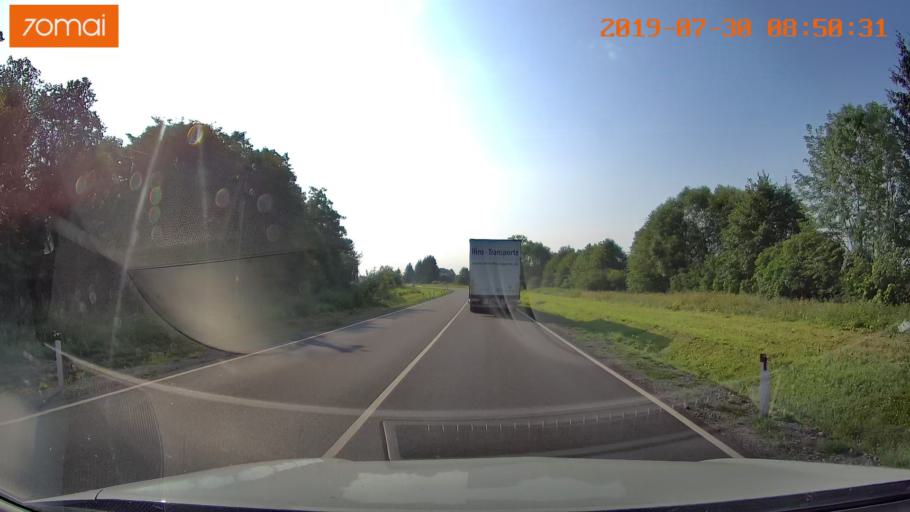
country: RU
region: Kaliningrad
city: Chernyakhovsk
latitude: 54.6069
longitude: 21.9409
